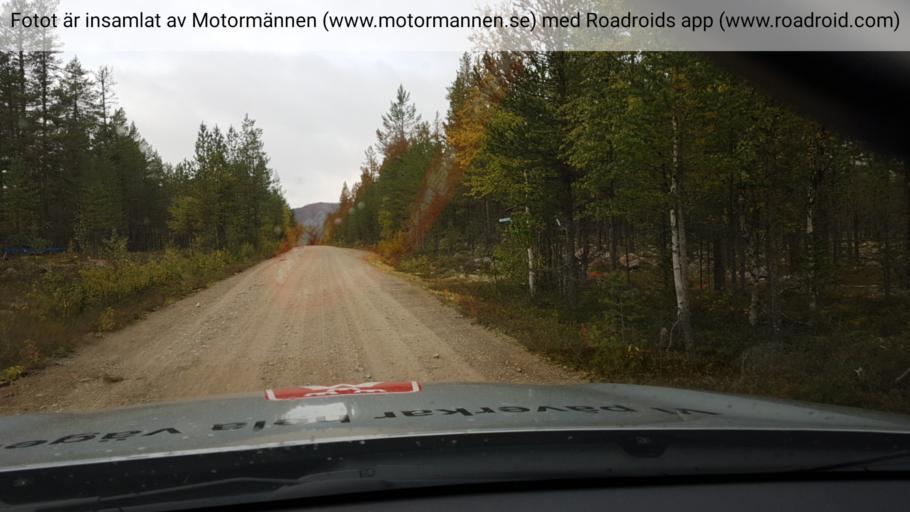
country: SE
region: Jaemtland
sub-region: Harjedalens Kommun
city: Sveg
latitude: 62.2423
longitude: 13.3227
